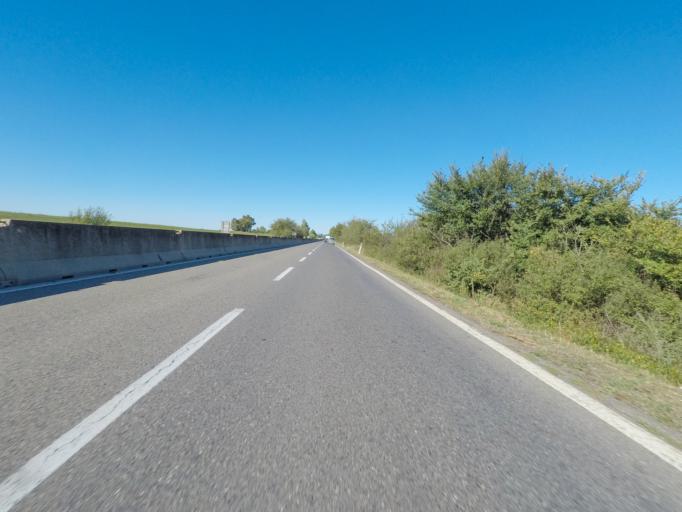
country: IT
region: Tuscany
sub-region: Provincia di Grosseto
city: Grosseto
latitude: 42.6938
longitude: 11.1380
